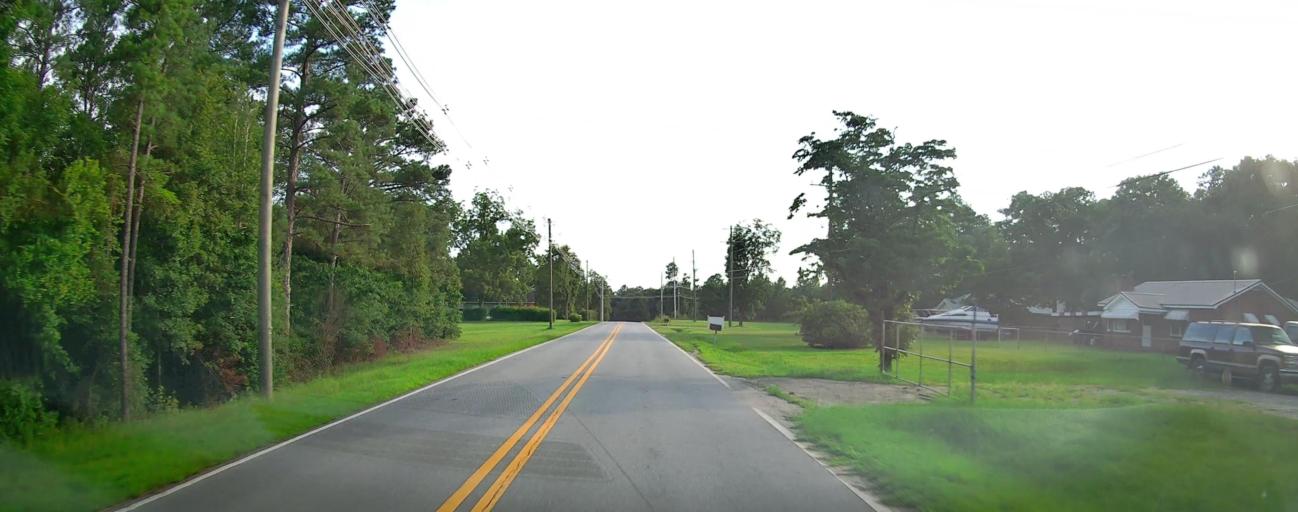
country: US
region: Georgia
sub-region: Bibb County
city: West Point
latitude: 32.7432
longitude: -83.7280
